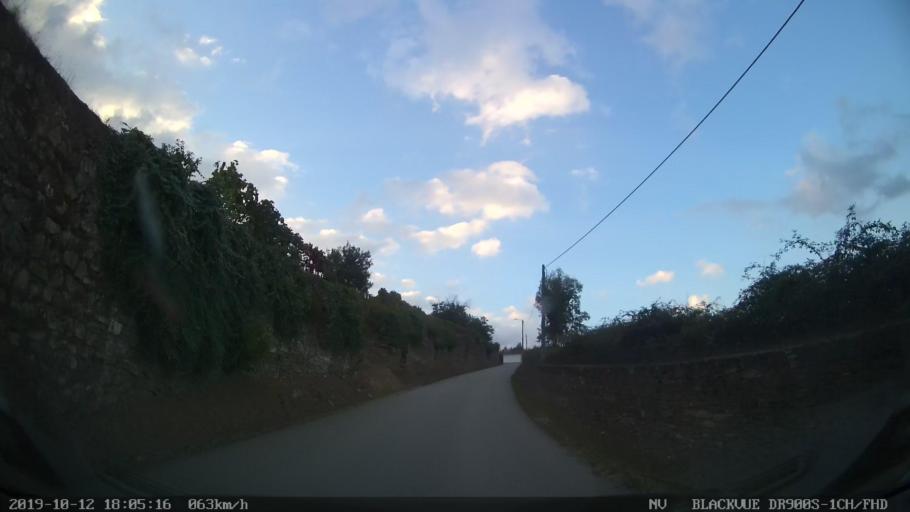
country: PT
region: Vila Real
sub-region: Mesao Frio
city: Mesao Frio
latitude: 41.1759
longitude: -7.8444
